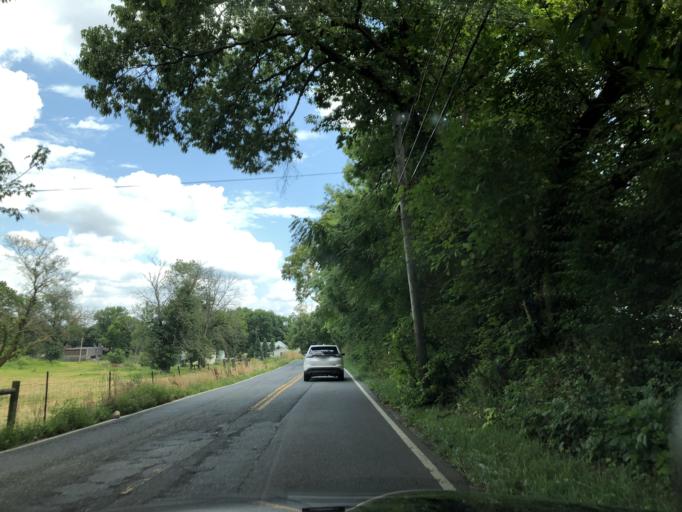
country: US
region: Maryland
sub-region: Frederick County
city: Clover Hill
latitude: 39.4296
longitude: -77.4432
